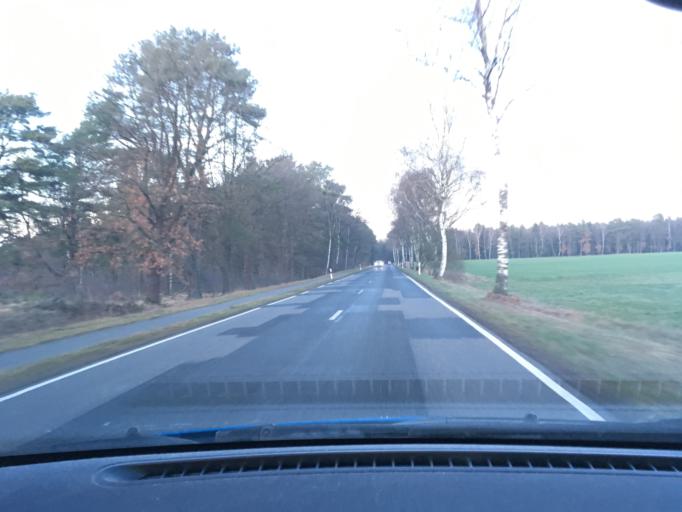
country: DE
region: Lower Saxony
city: Handeloh
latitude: 53.2447
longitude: 9.8708
